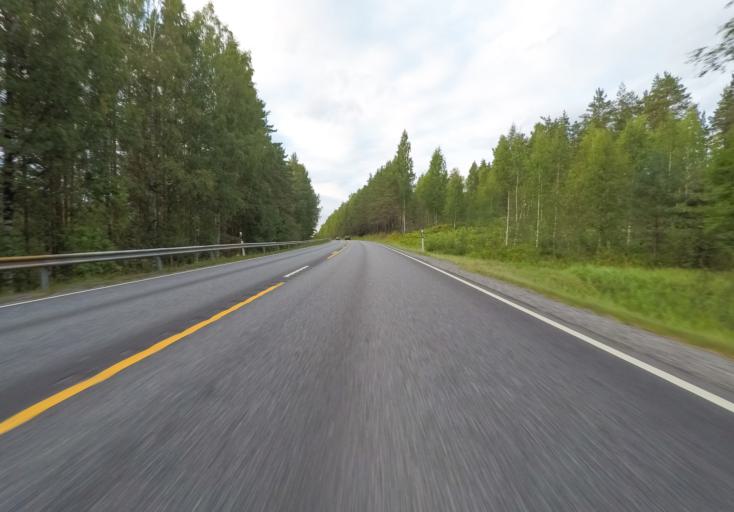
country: FI
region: Paijanne Tavastia
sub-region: Lahti
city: Hartola
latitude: 61.6491
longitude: 26.0288
